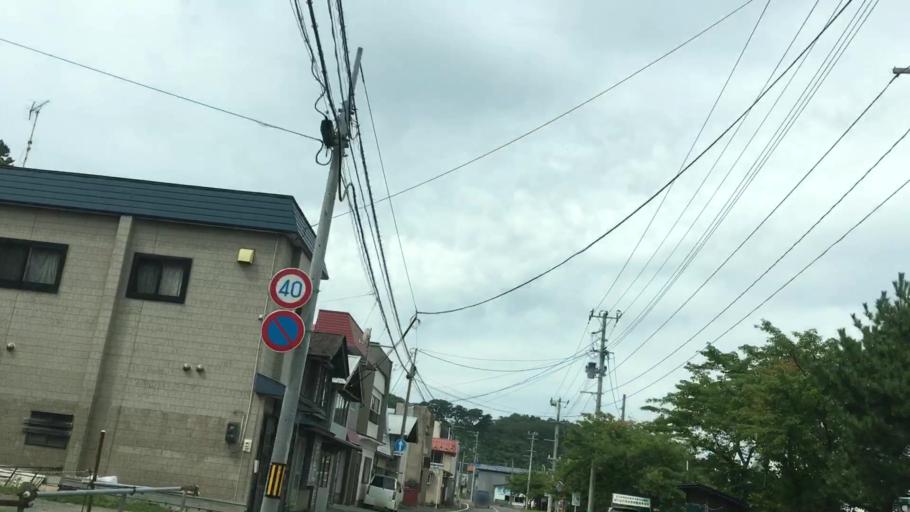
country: JP
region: Aomori
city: Shimokizukuri
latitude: 40.7783
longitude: 140.2116
